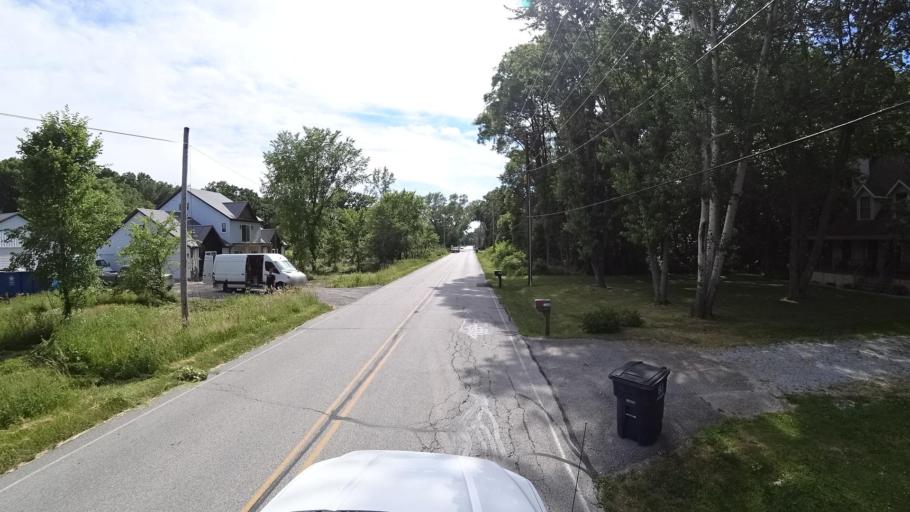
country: US
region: Indiana
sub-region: Porter County
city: Porter
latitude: 41.6088
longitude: -87.0891
